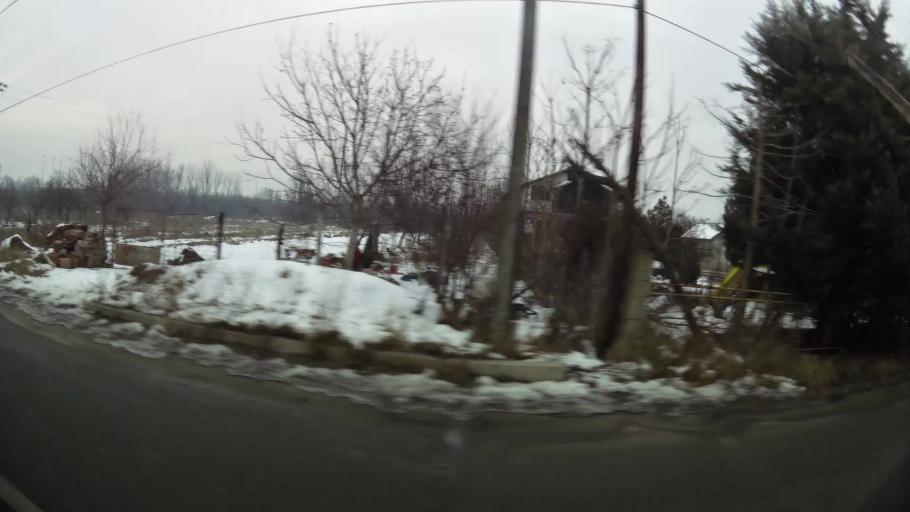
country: MK
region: Cucer-Sandevo
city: Chucher - Sandevo
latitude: 42.0517
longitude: 21.3648
